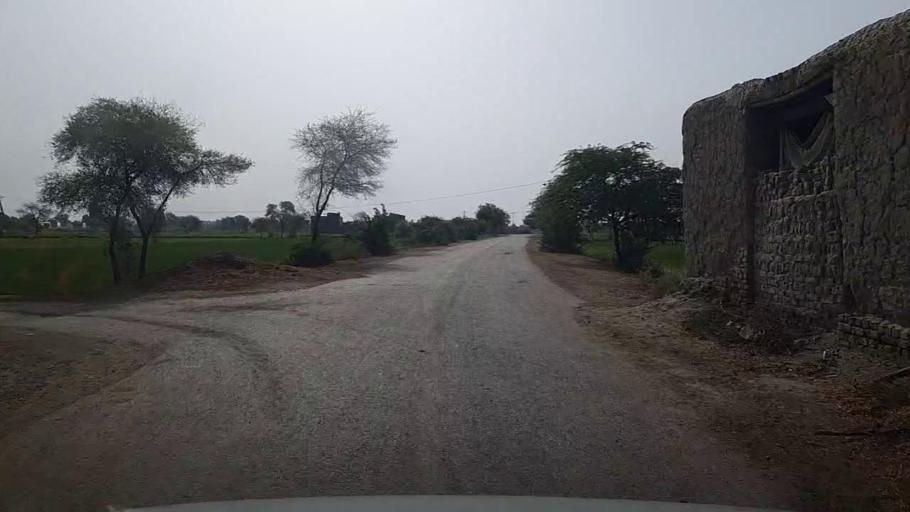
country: PK
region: Sindh
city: Mehar
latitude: 27.1212
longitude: 67.8161
